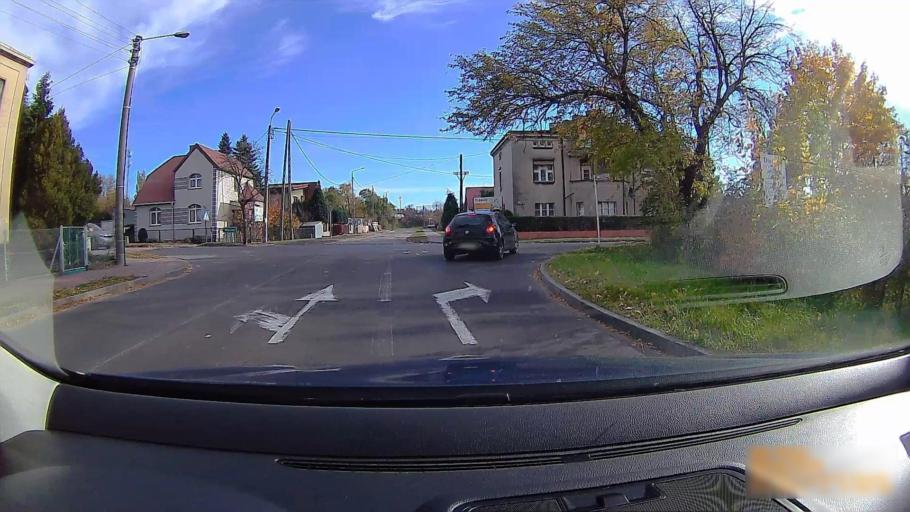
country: PL
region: Greater Poland Voivodeship
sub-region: Powiat ostrzeszowski
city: Ostrzeszow
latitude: 51.4320
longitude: 17.9355
